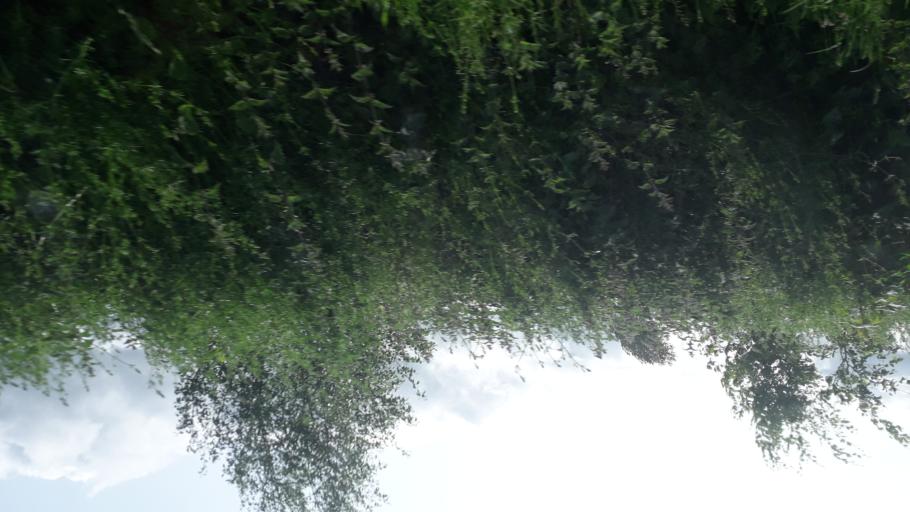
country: IE
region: Leinster
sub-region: Kilkenny
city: Graiguenamanagh
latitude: 52.6060
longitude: -7.0102
